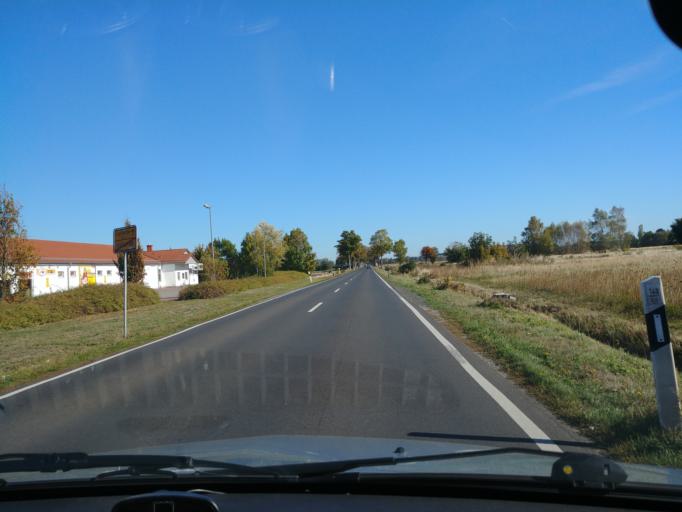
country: DE
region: Lower Saxony
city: Hillerse
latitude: 52.4166
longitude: 10.4107
